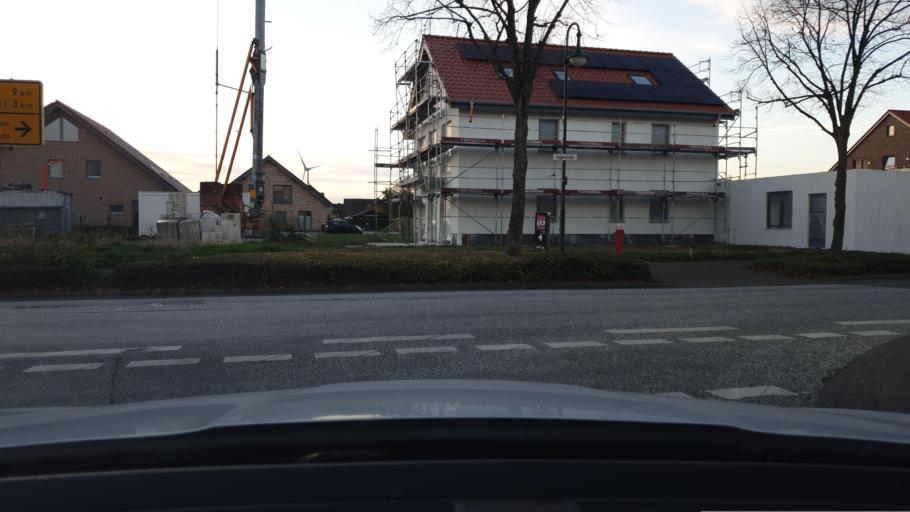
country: DE
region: North Rhine-Westphalia
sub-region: Regierungsbezirk Detmold
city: Werther
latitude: 52.0979
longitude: 8.4531
